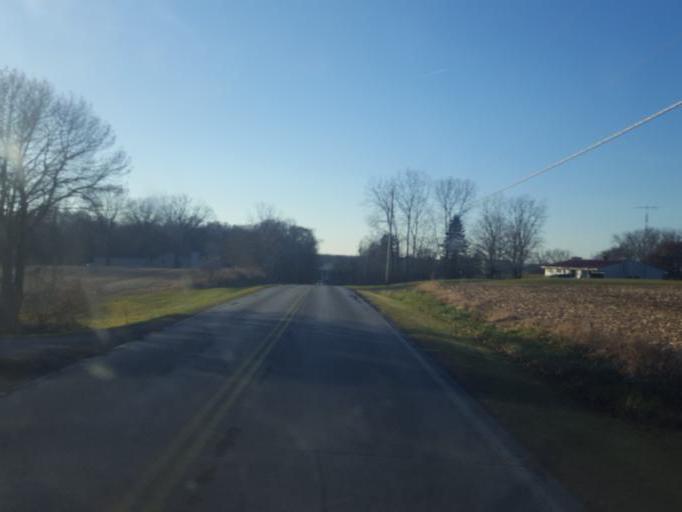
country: US
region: Ohio
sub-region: Wayne County
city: Shreve
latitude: 40.8070
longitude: -82.0850
